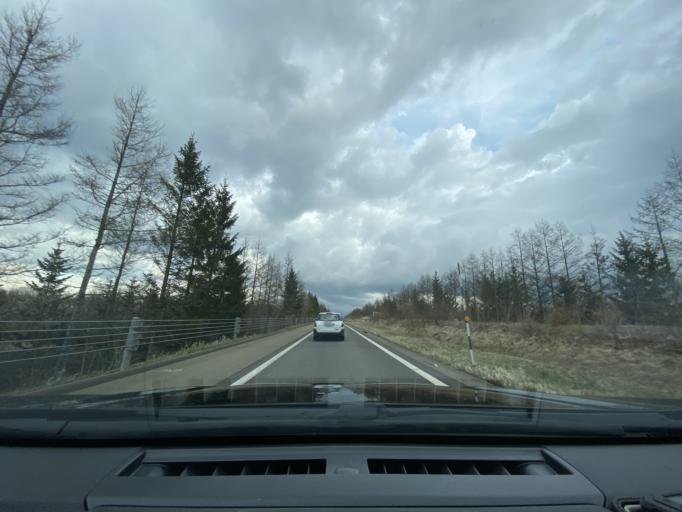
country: JP
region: Hokkaido
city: Otofuke
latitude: 42.9795
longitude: 143.1600
